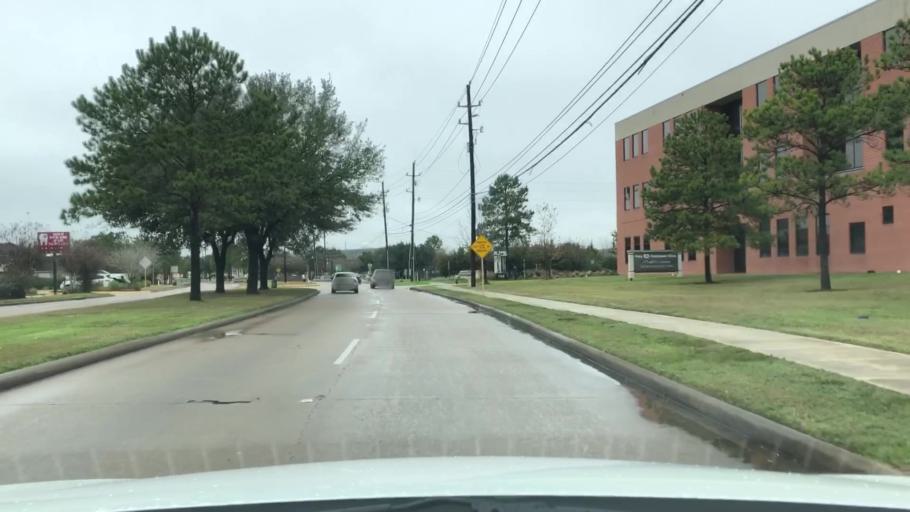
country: US
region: Texas
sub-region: Fort Bend County
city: Cinco Ranch
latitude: 29.7762
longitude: -95.7362
